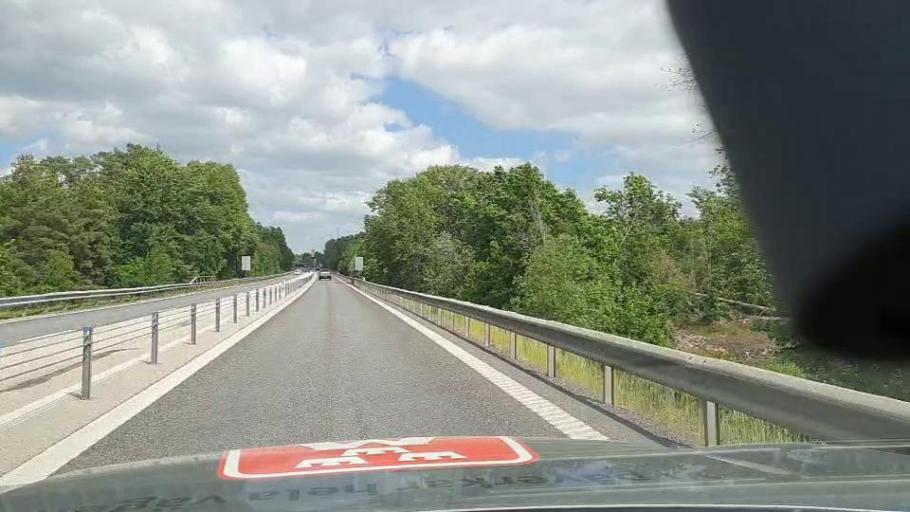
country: SE
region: Blekinge
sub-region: Ronneby Kommun
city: Ronneby
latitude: 56.2182
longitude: 15.1985
